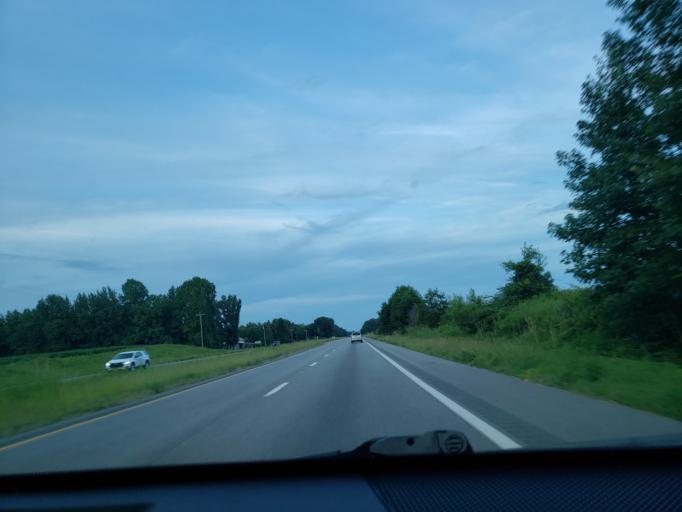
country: US
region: Virginia
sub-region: Southampton County
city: Courtland
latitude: 36.7040
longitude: -77.2199
